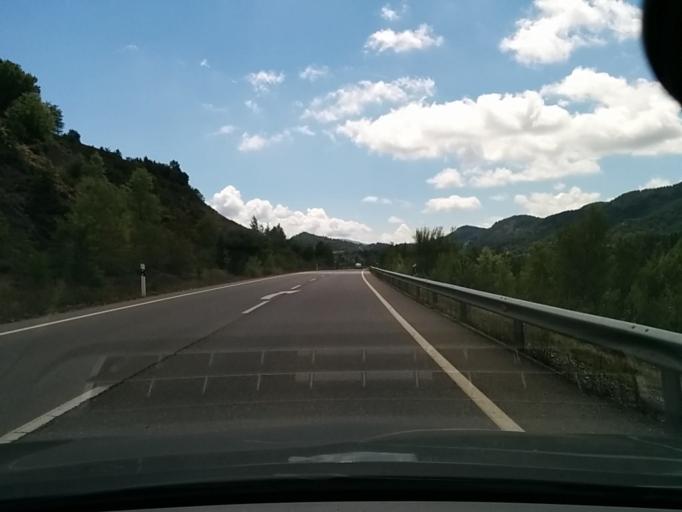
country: ES
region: Aragon
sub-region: Provincia de Huesca
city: Ainsa
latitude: 42.4220
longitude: 0.1268
